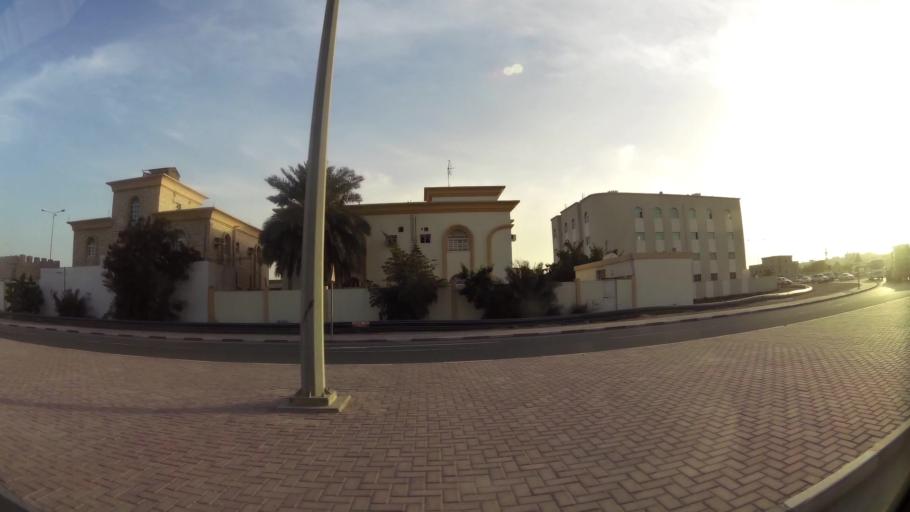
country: QA
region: Al Wakrah
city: Al Wakrah
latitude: 25.1505
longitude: 51.6030
